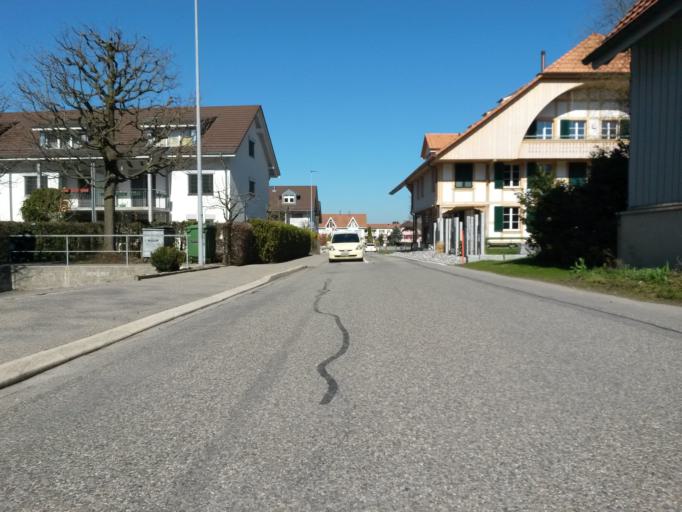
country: CH
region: Bern
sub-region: Bern-Mittelland District
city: Zollikofen
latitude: 47.0135
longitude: 7.4770
